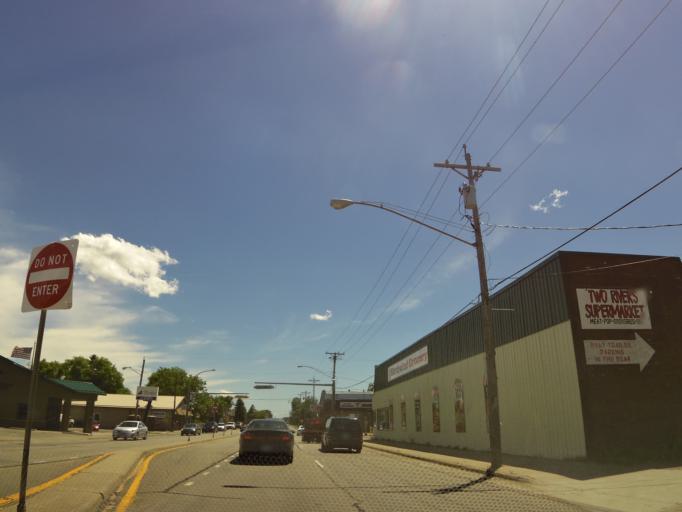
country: US
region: Minnesota
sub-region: Todd County
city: Staples
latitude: 46.3371
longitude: -94.6461
